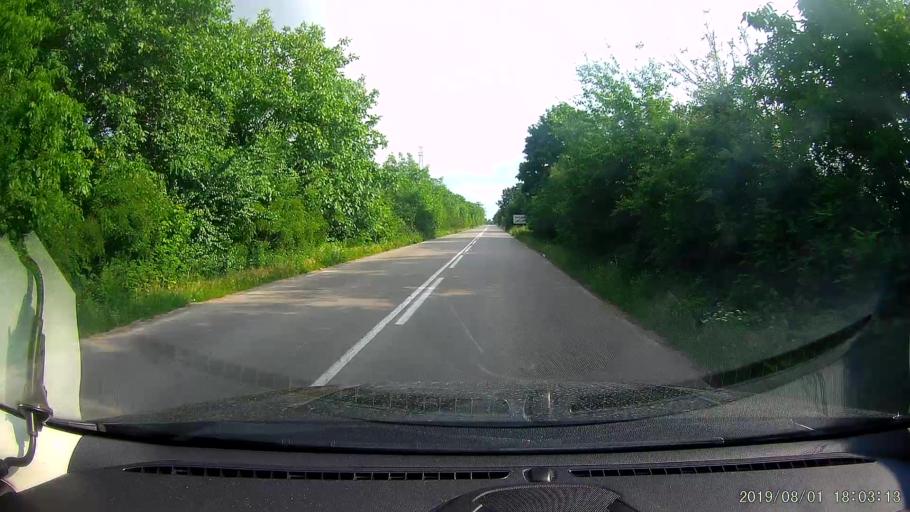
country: BG
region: Silistra
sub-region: Obshtina Alfatar
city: Alfatar
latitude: 43.9324
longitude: 27.2902
